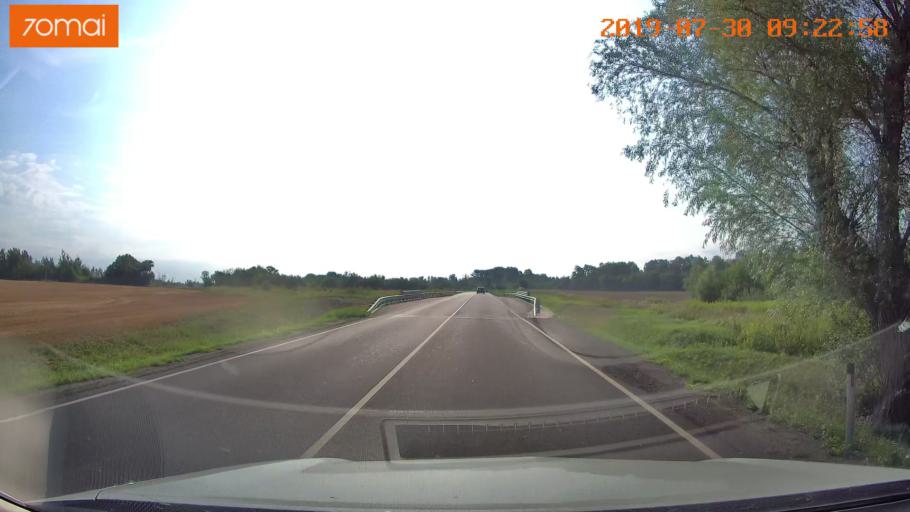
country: RU
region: Kaliningrad
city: Nesterov
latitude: 54.6331
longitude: 22.6658
